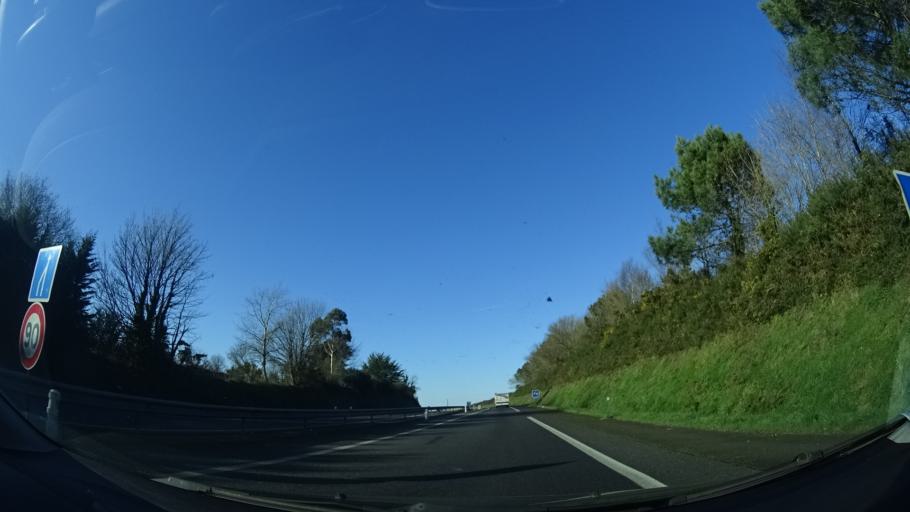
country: FR
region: Brittany
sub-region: Departement du Finistere
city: Henvic
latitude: 48.6445
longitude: -3.9401
